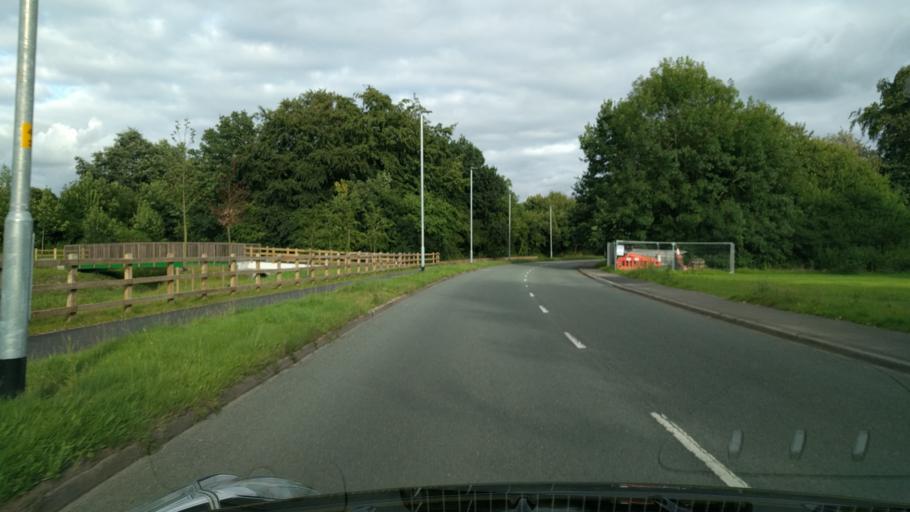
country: GB
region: England
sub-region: Warrington
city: Croft
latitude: 53.4218
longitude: -2.5588
